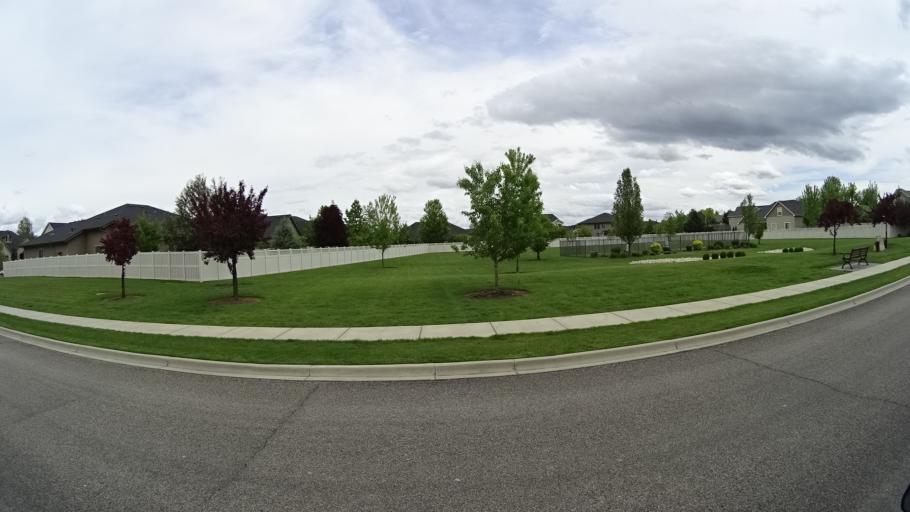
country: US
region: Idaho
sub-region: Ada County
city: Meridian
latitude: 43.6402
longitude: -116.4243
